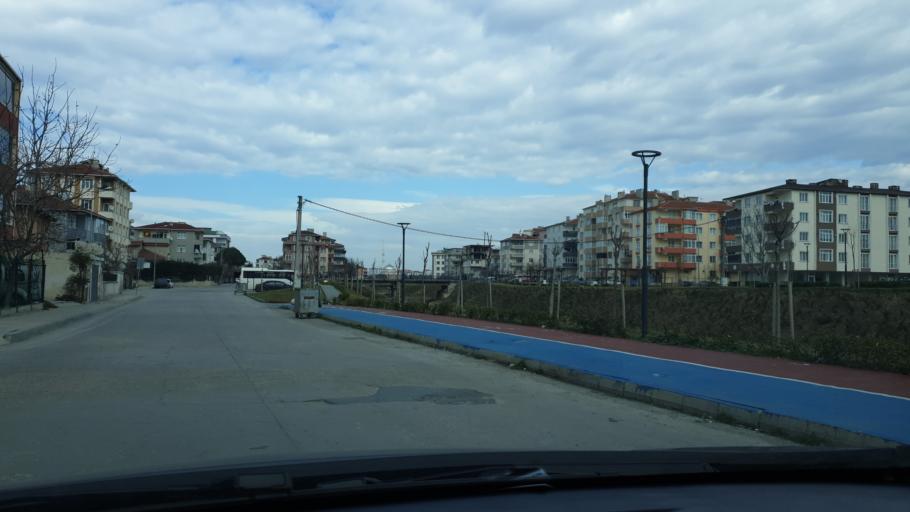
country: TR
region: Tekirdag
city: Cerkezkoey
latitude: 41.2842
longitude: 28.0038
